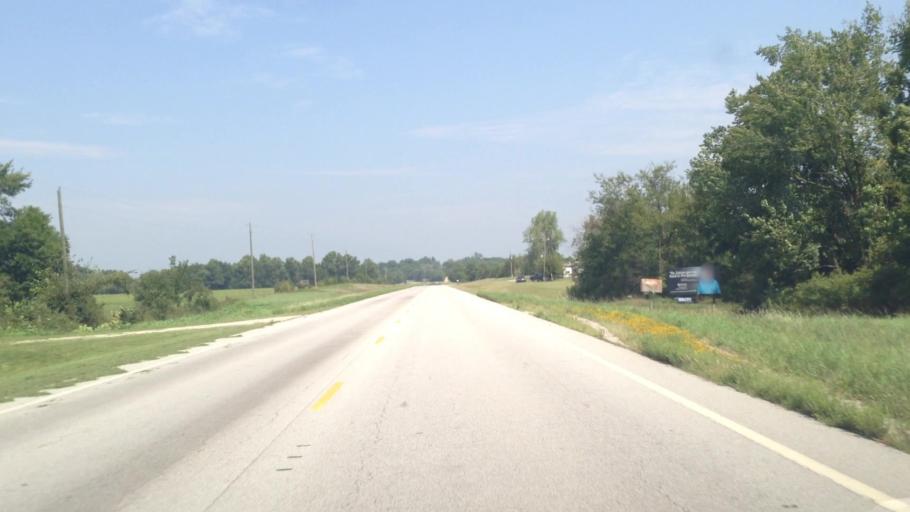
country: US
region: Kansas
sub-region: Labette County
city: Oswego
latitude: 37.1377
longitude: -95.1034
